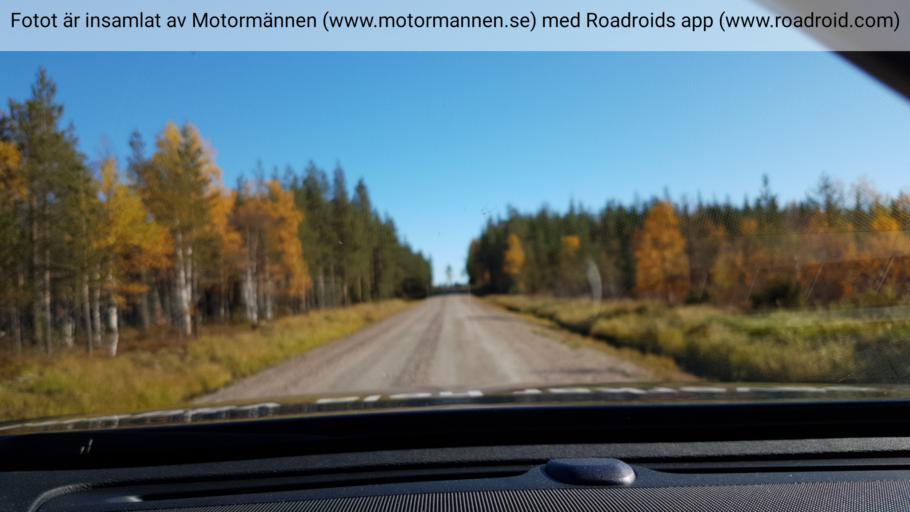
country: SE
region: Norrbotten
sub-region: Gallivare Kommun
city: Gaellivare
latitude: 66.5720
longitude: 21.0722
